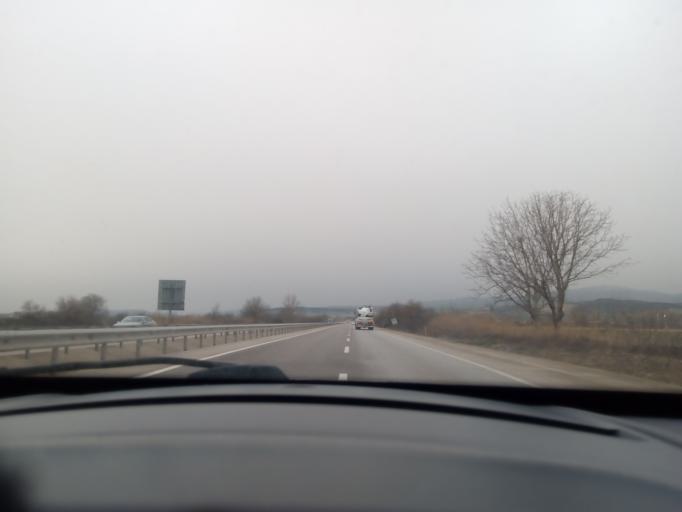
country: TR
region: Balikesir
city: Gobel
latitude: 39.9857
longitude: 28.1954
